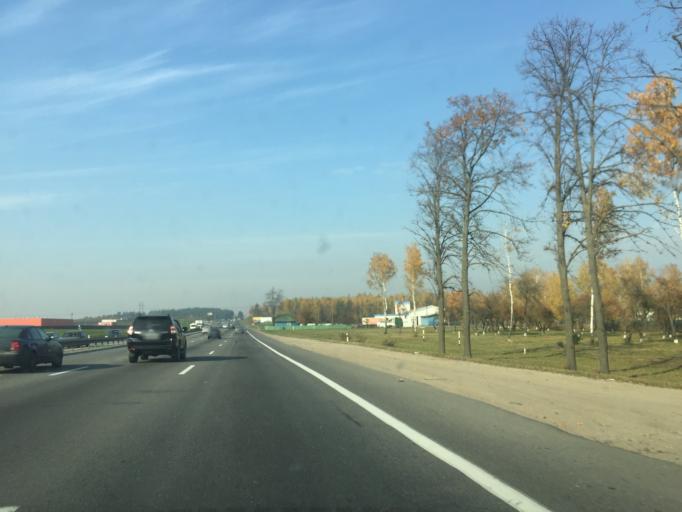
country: BY
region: Minsk
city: Pryvol'ny
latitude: 53.8082
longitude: 27.7868
